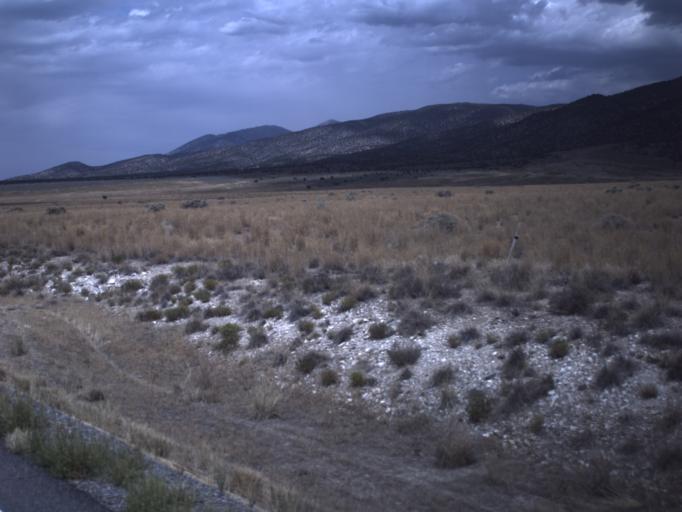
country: US
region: Utah
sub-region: Utah County
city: Eagle Mountain
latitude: 40.2663
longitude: -112.2387
